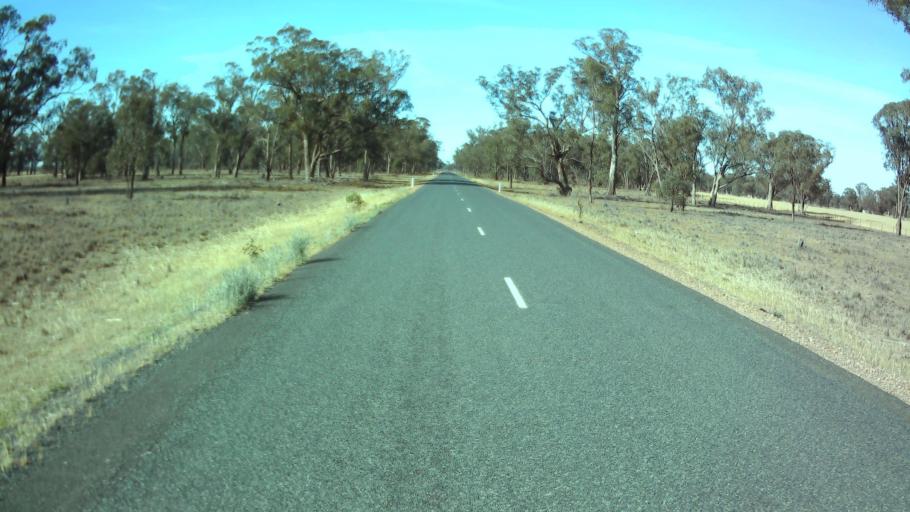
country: AU
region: New South Wales
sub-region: Weddin
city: Grenfell
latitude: -34.0607
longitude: 147.9099
